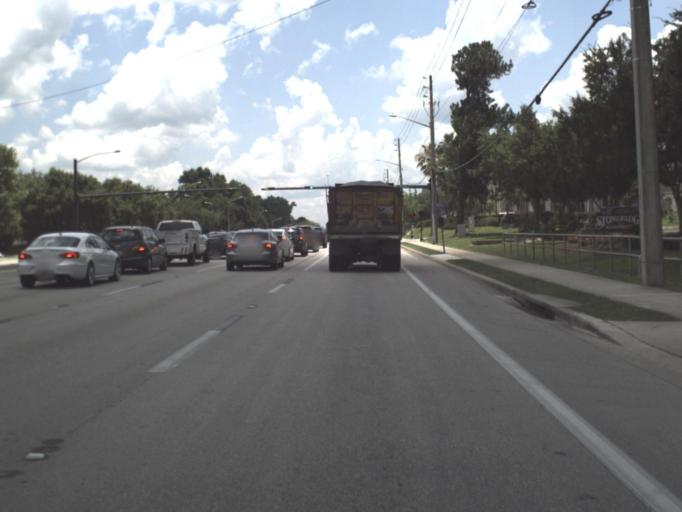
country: US
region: Florida
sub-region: Alachua County
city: Gainesville
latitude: 29.6190
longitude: -82.3727
